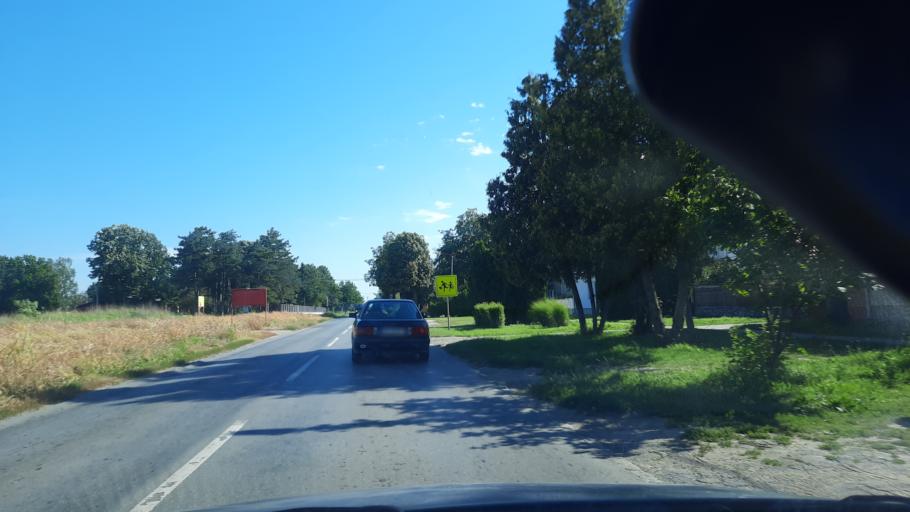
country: RS
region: Autonomna Pokrajina Vojvodina
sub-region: Juznobanatski Okrug
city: Kovin
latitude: 44.7616
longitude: 20.9864
